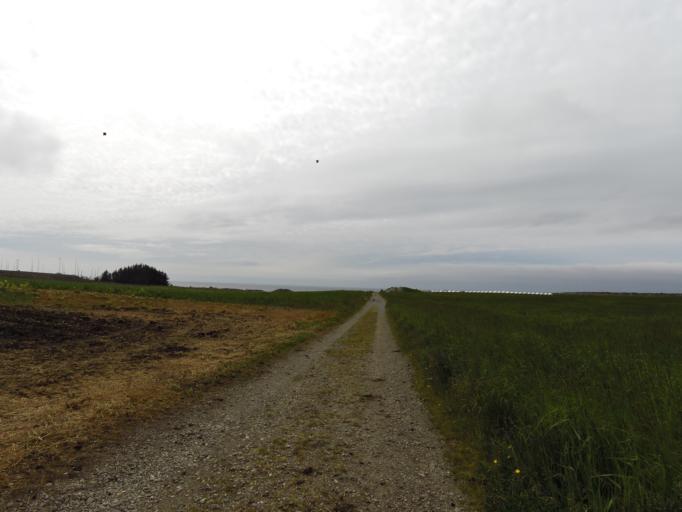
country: NO
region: Rogaland
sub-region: Ha
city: Naerbo
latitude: 58.6340
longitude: 5.5960
